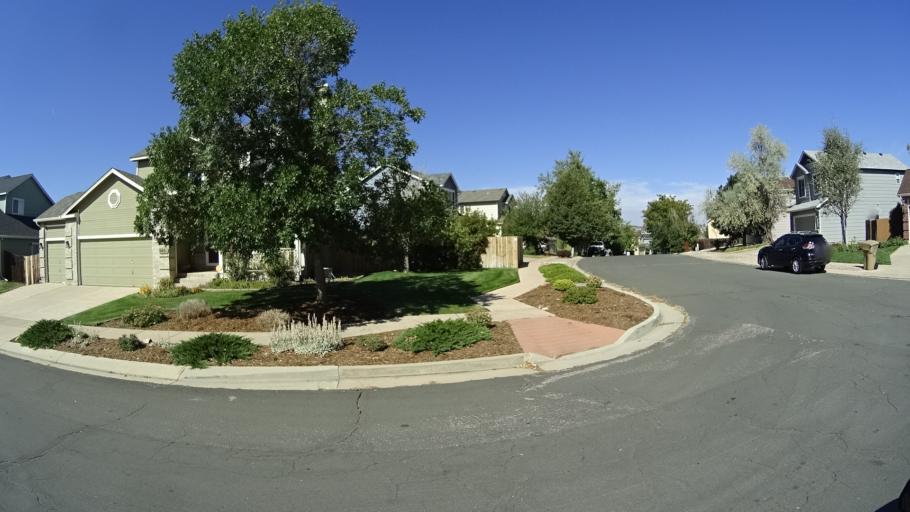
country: US
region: Colorado
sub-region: El Paso County
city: Cimarron Hills
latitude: 38.8824
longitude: -104.7014
